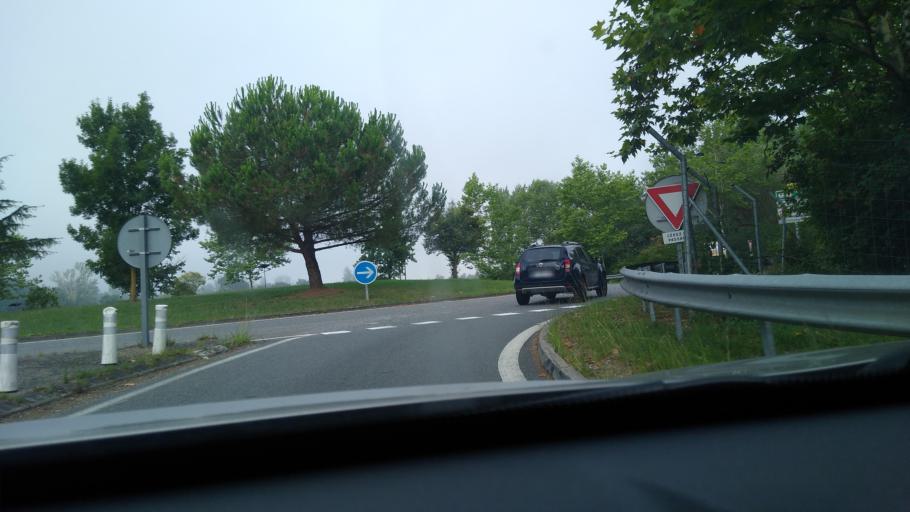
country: FR
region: Midi-Pyrenees
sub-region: Departement de la Haute-Garonne
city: Salies-du-Salat
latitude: 43.1233
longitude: 0.9365
